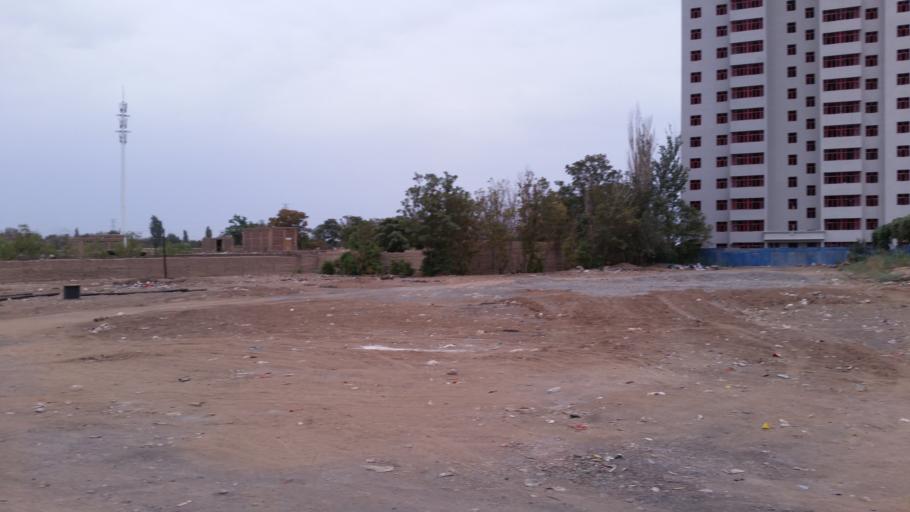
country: CN
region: Xinjiang Uygur Zizhiqu
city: Laochenglu
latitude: 42.9476
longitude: 89.1964
